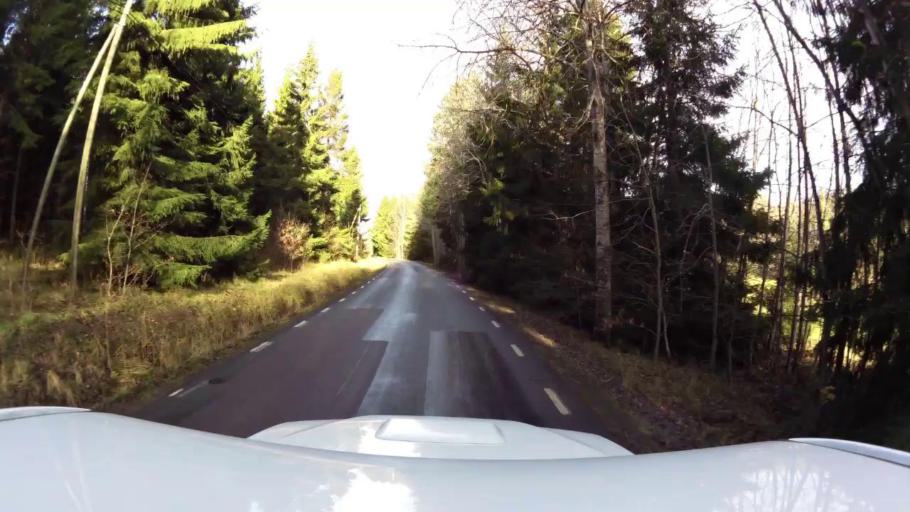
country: SE
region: OEstergoetland
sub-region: Linkopings Kommun
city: Sturefors
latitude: 58.3342
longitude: 15.6528
